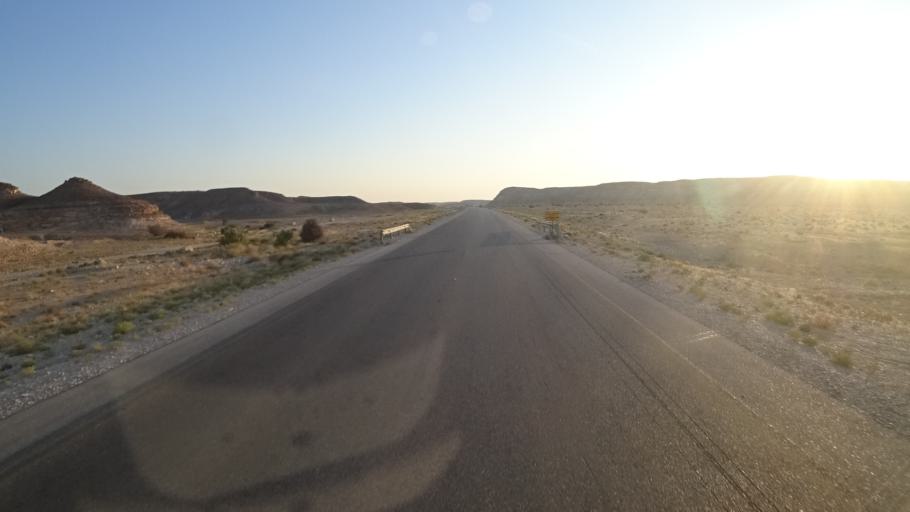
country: OM
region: Zufar
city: Salalah
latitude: 17.5288
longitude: 53.3816
